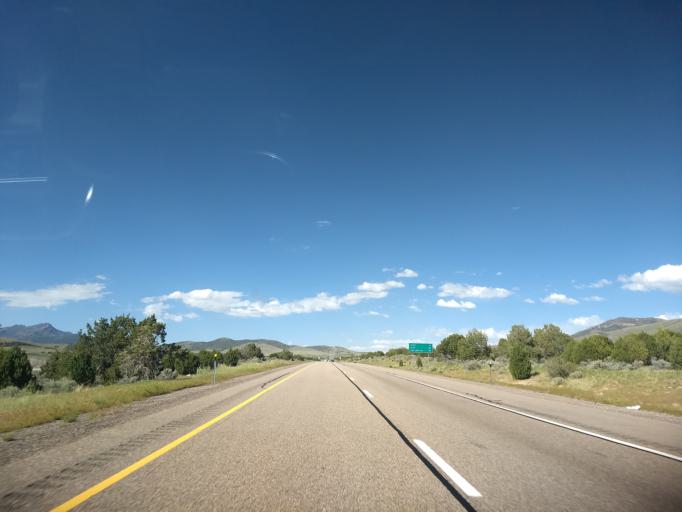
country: US
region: Utah
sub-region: Millard County
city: Fillmore
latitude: 39.1566
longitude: -112.2265
